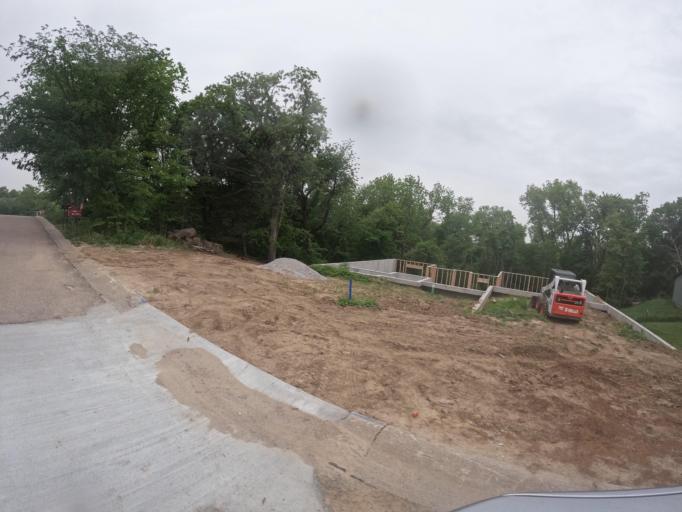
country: US
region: Nebraska
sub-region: Sarpy County
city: Offutt Air Force Base
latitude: 41.0520
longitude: -95.9687
